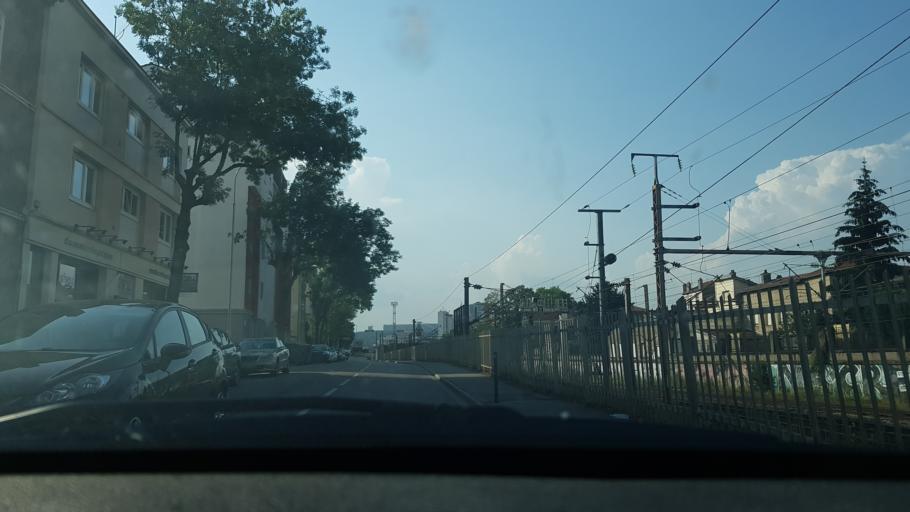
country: FR
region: Lorraine
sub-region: Departement de Meurthe-et-Moselle
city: Nancy
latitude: 48.6807
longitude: 6.1876
